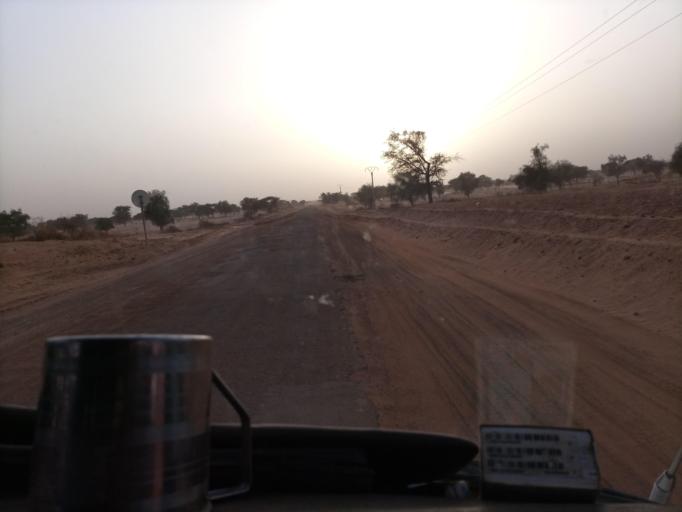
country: SN
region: Louga
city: Dara
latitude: 15.4066
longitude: -15.6703
